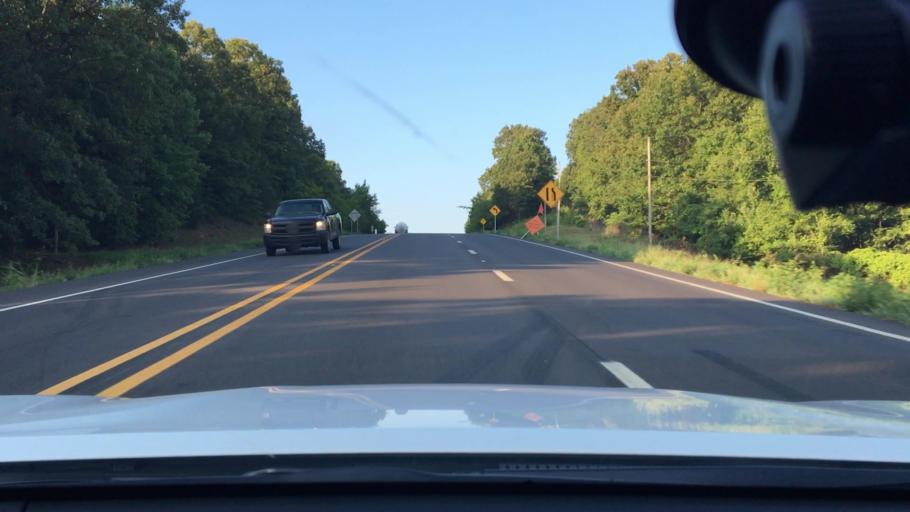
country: US
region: Arkansas
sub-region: Johnson County
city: Clarksville
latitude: 35.4209
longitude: -93.5309
